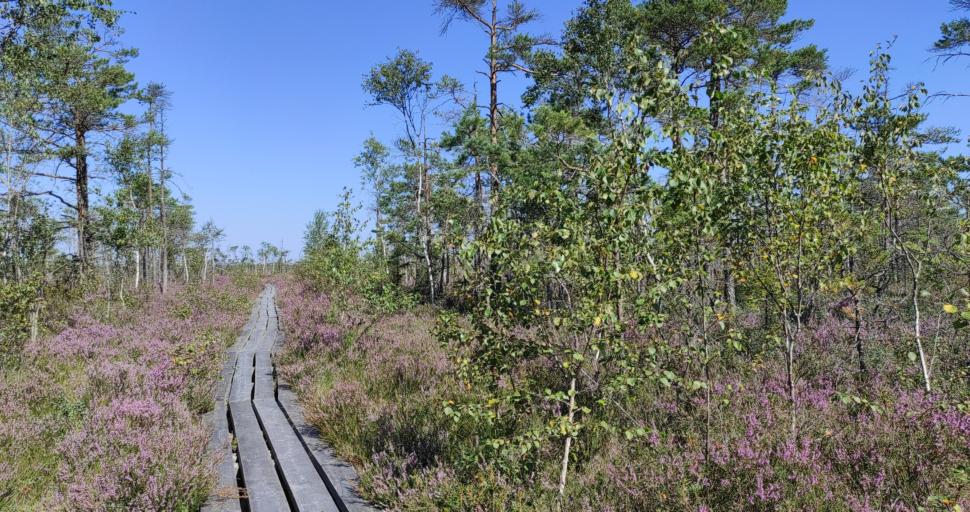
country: LT
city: Skuodas
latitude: 56.2489
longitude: 21.3960
